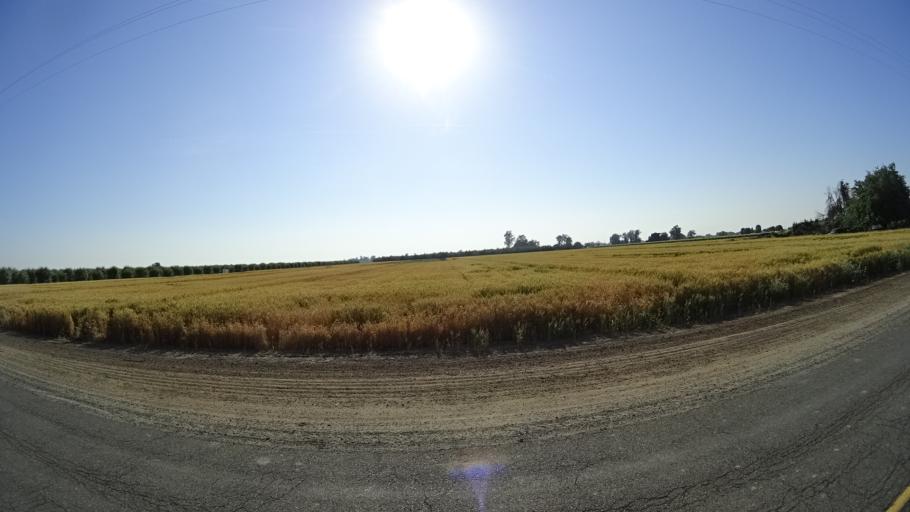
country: US
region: California
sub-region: Fresno County
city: Riverdale
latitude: 36.3706
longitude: -119.8693
